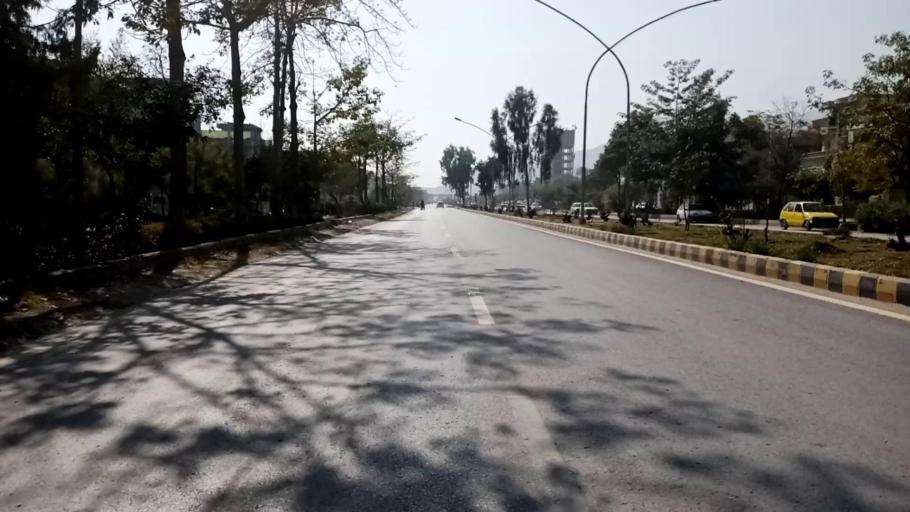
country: PK
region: Khyber Pakhtunkhwa
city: Peshawar
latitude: 33.9541
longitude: 71.4330
